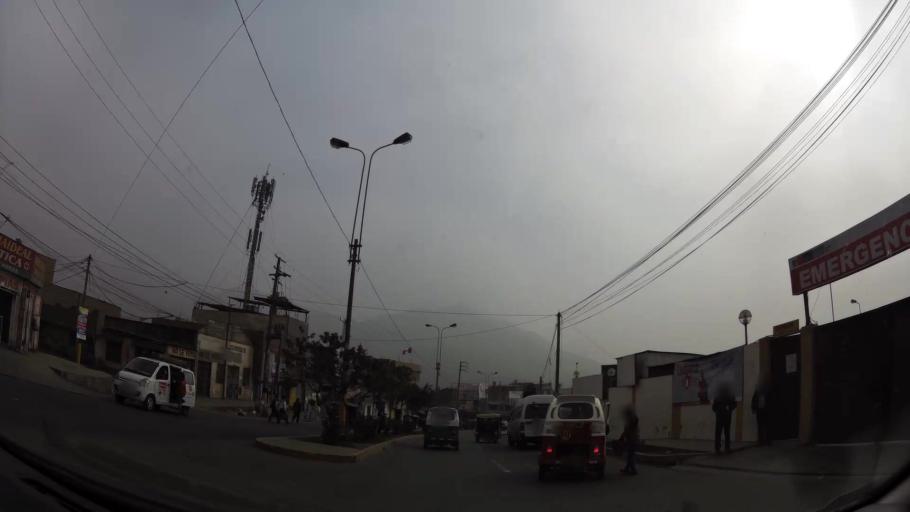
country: PE
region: Lima
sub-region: Lima
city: Chaclacayo
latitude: -12.0160
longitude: -76.8199
